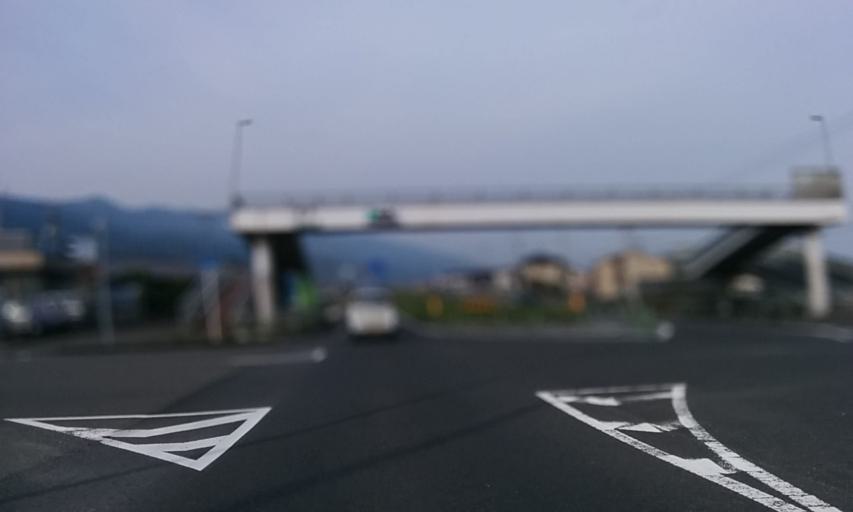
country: JP
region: Ehime
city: Kawanoecho
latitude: 33.9771
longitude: 133.5478
